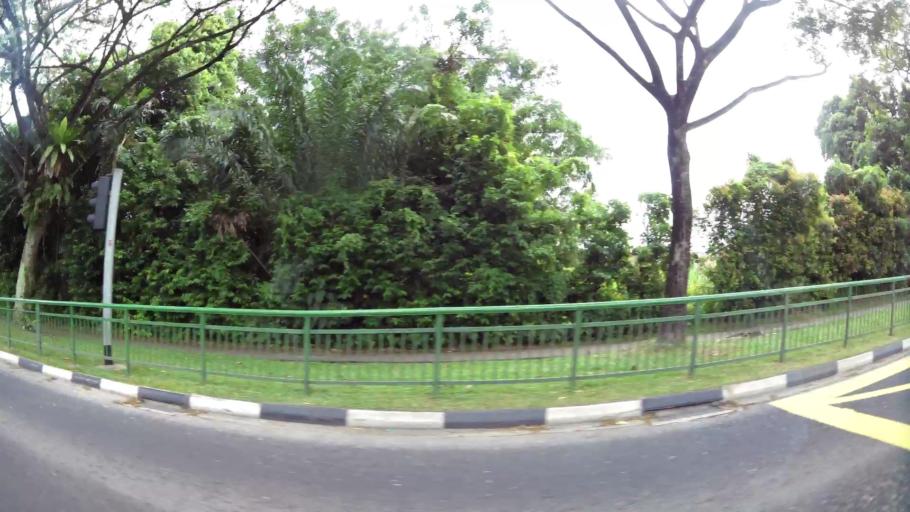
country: SG
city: Singapore
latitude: 1.3259
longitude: 103.7643
